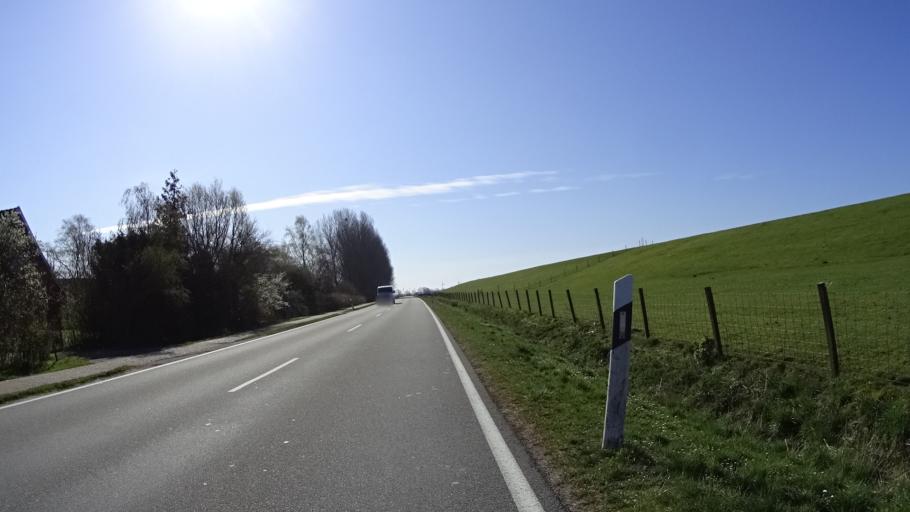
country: DE
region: Lower Saxony
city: Jemgum
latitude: 53.2910
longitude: 7.4019
